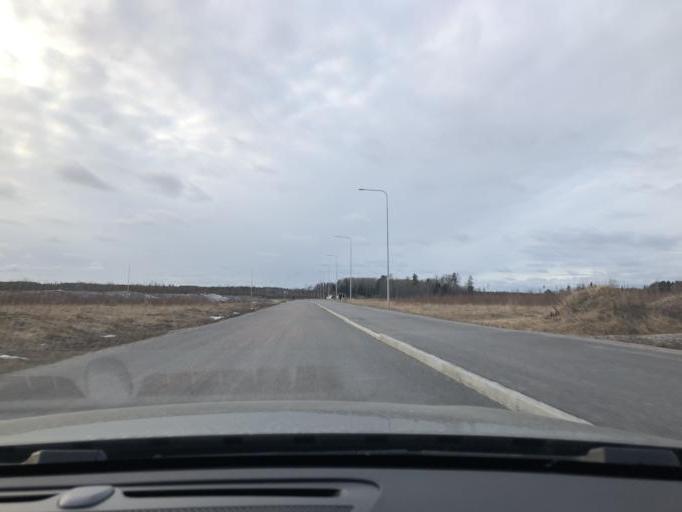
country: SE
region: Uppsala
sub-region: Tierps Kommun
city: Tierp
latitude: 60.3510
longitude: 17.4927
